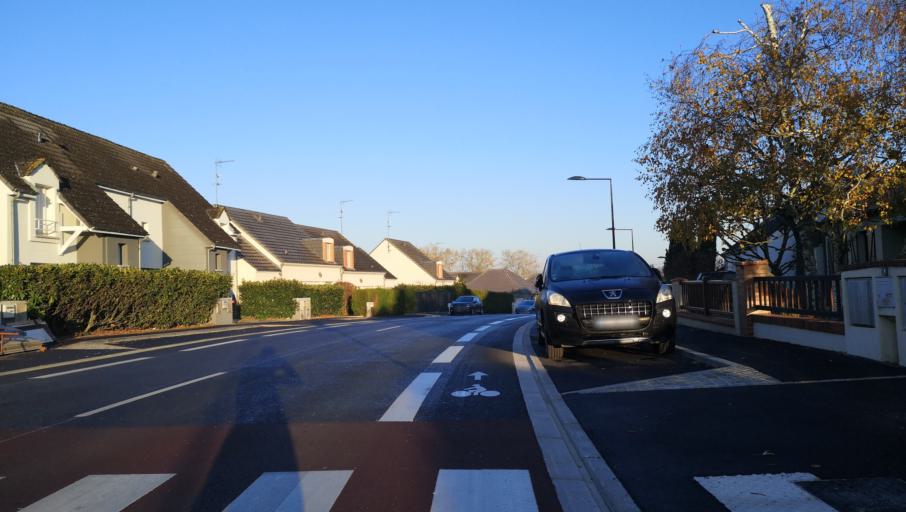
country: FR
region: Centre
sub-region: Departement du Loiret
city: Saran
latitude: 47.9341
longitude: 1.8900
